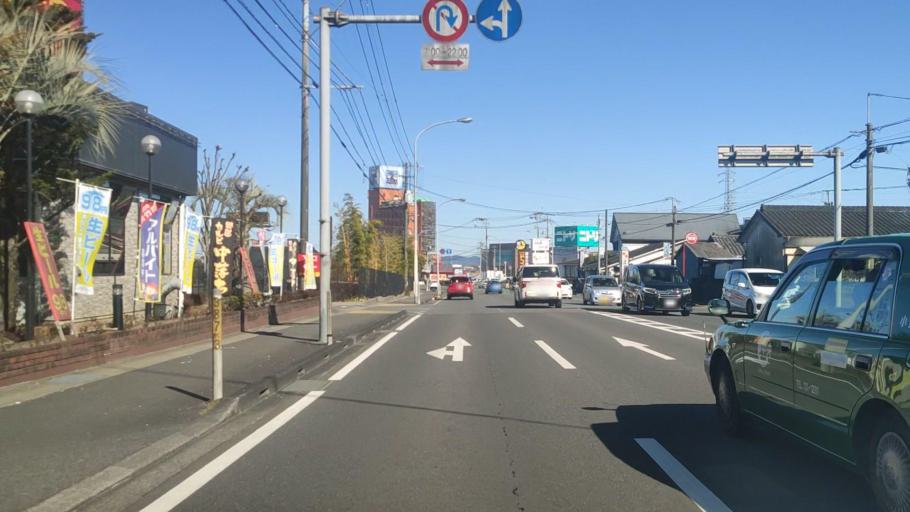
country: JP
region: Miyazaki
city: Miyakonojo
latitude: 31.7457
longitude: 131.0767
